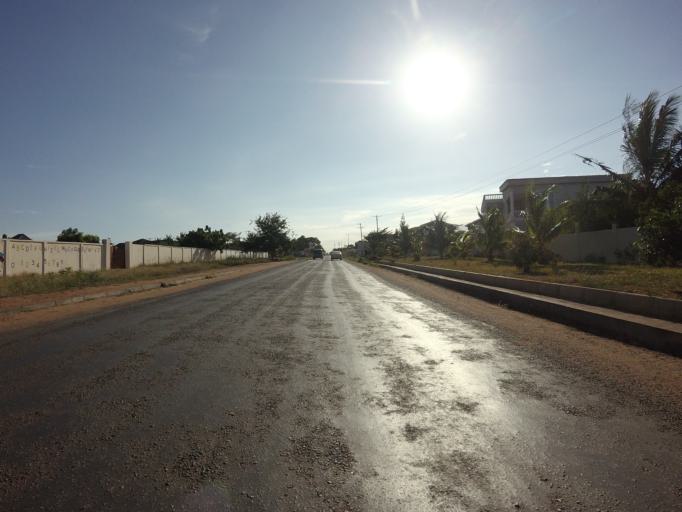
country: GH
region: Greater Accra
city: Nungua
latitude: 5.6510
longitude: -0.0701
